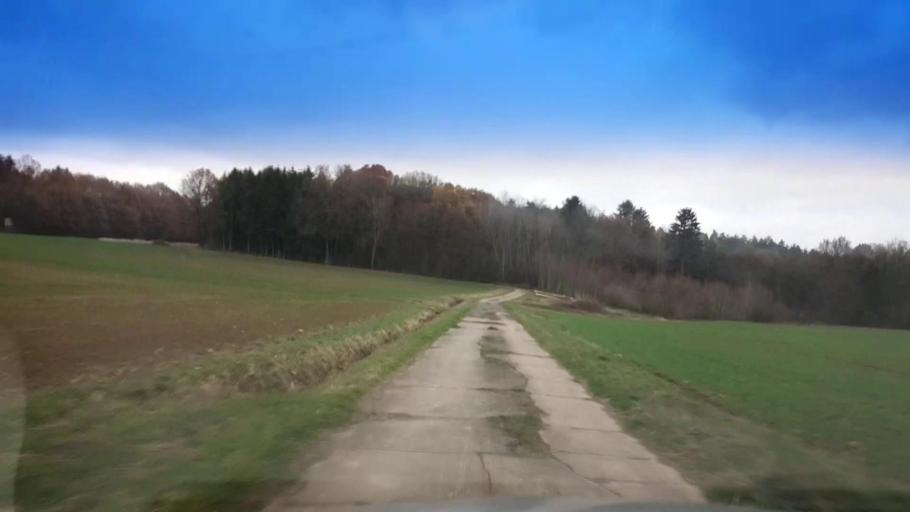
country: DE
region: Bavaria
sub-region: Upper Franconia
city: Zapfendorf
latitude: 49.9815
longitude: 10.9533
